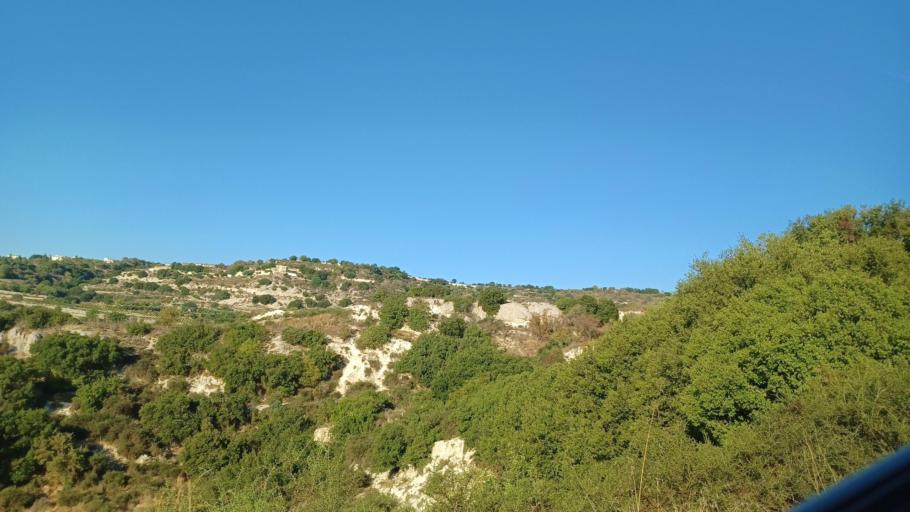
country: CY
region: Pafos
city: Mesogi
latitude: 34.8535
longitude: 32.5060
